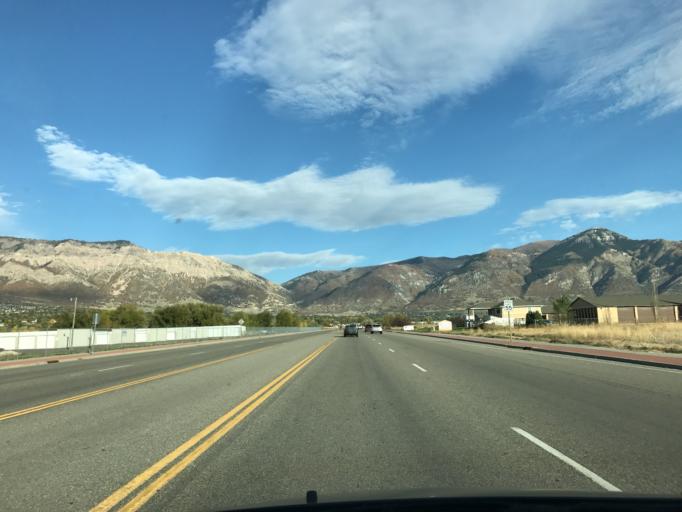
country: US
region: Utah
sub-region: Weber County
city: Pleasant View
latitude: 41.3068
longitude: -112.0027
